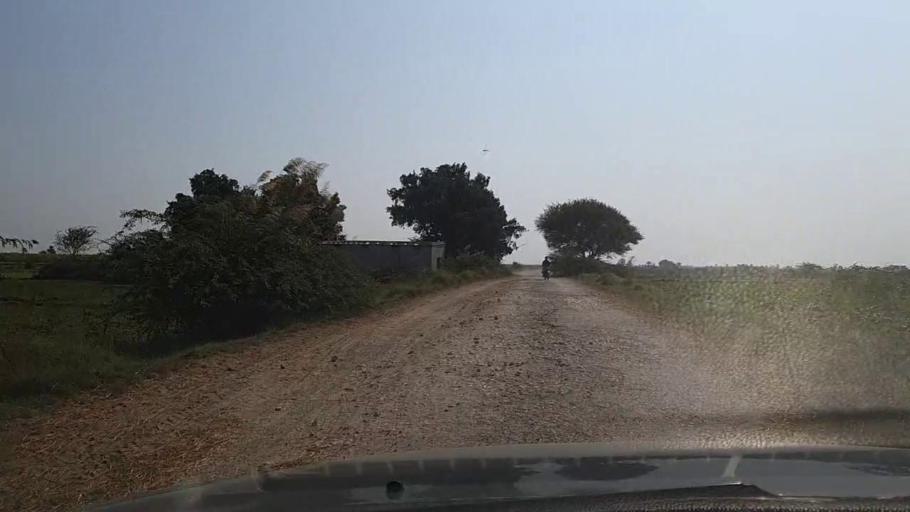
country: PK
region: Sindh
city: Mirpur Sakro
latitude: 24.3913
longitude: 67.6650
